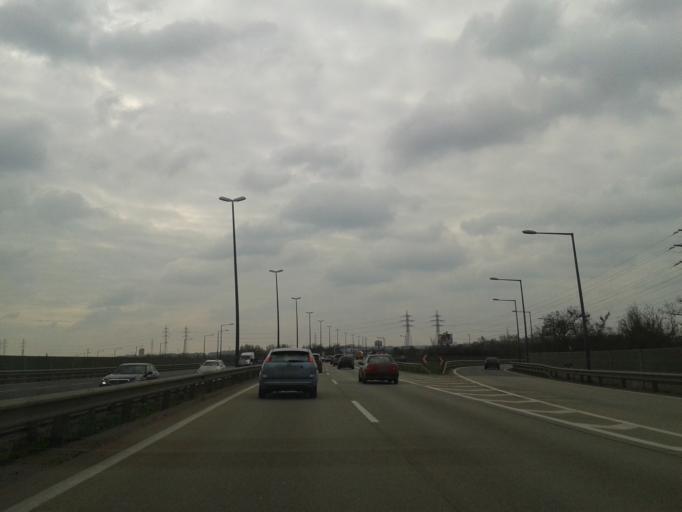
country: AT
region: Lower Austria
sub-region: Politischer Bezirk Wien-Umgebung
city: Schwechat
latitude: 48.1765
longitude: 16.4542
